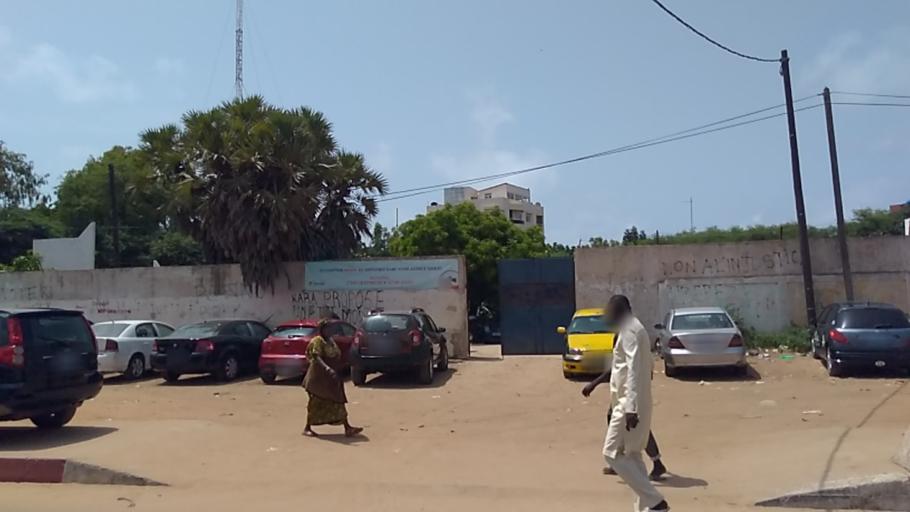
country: SN
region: Dakar
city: Mermoz Boabab
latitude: 14.7187
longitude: -17.4885
